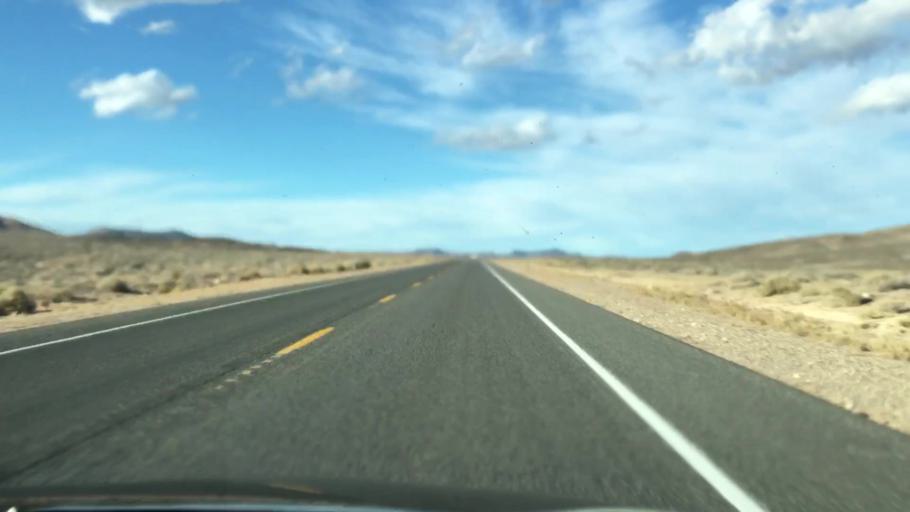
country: US
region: Nevada
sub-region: Esmeralda County
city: Goldfield
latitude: 37.5329
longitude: -117.1930
